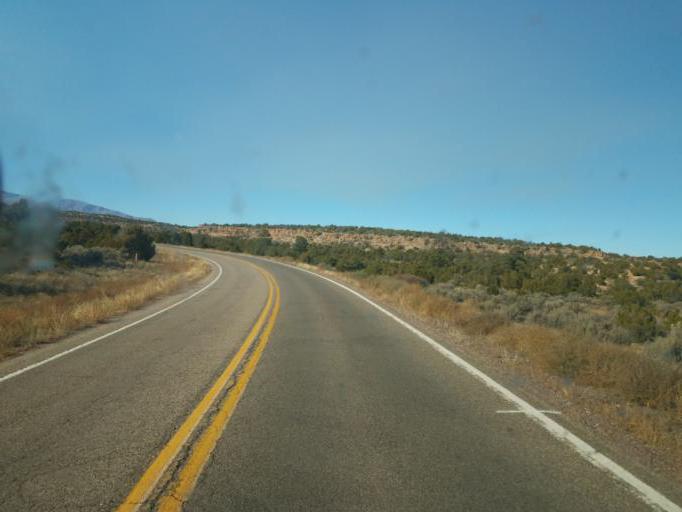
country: US
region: New Mexico
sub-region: Los Alamos County
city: White Rock
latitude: 35.8335
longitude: -106.2006
